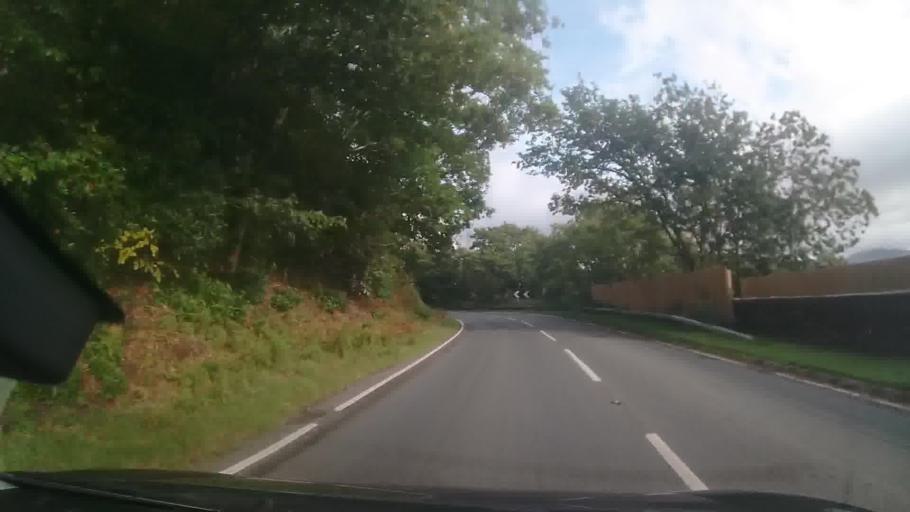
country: GB
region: Wales
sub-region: Gwynedd
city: Barmouth
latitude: 52.7369
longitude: -4.0219
